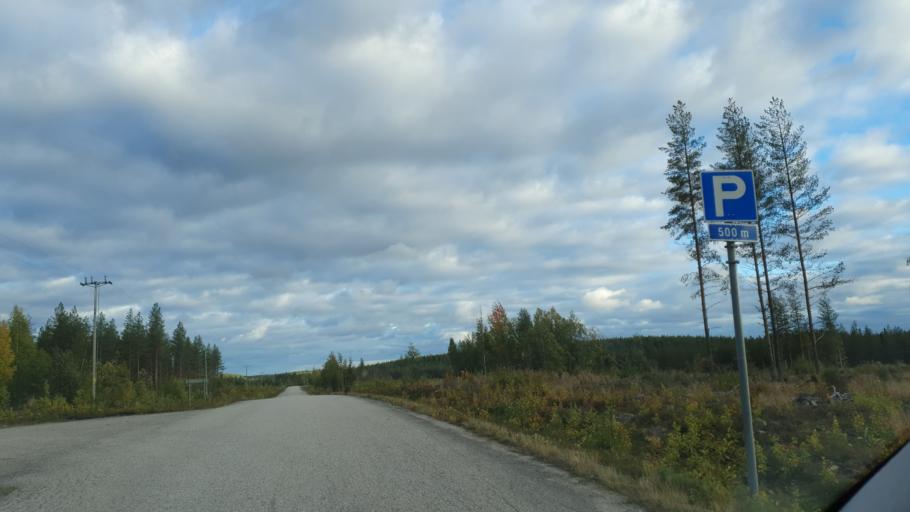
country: FI
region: North Karelia
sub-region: Pielisen Karjala
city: Lieksa
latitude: 63.9198
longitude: 30.1603
